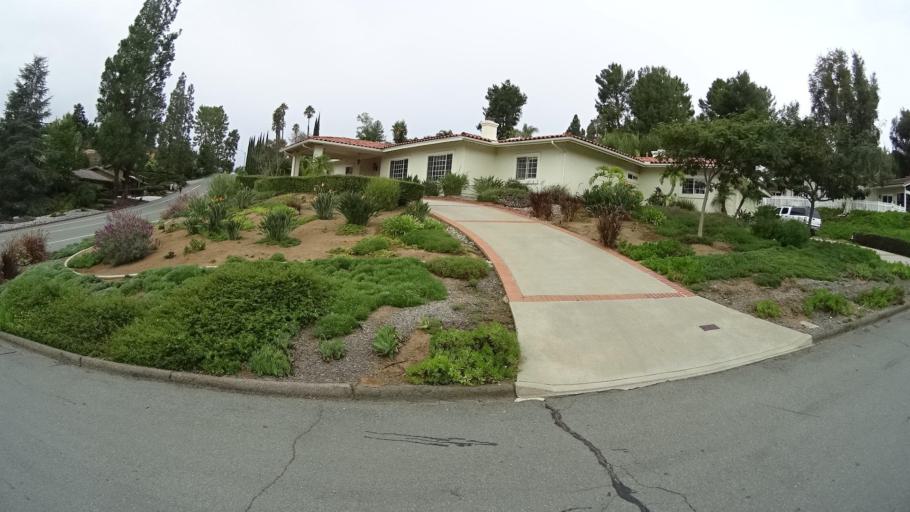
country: US
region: California
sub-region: San Diego County
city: Granite Hills
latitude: 32.7741
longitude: -116.9117
